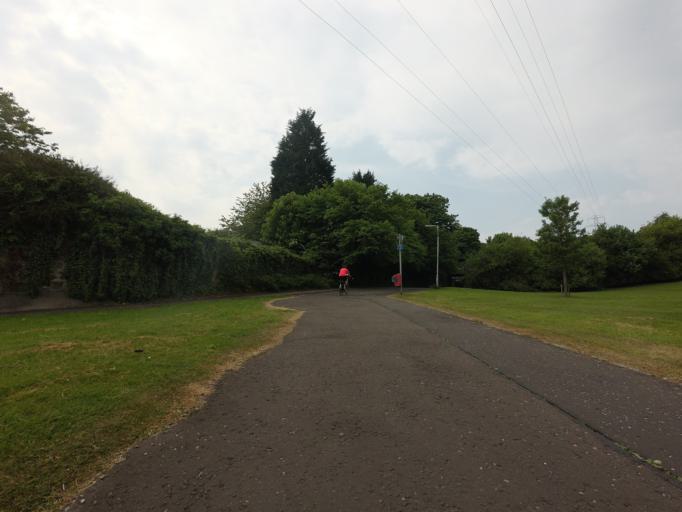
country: GB
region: Scotland
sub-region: Fife
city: Townhill
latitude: 56.0789
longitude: -3.4230
